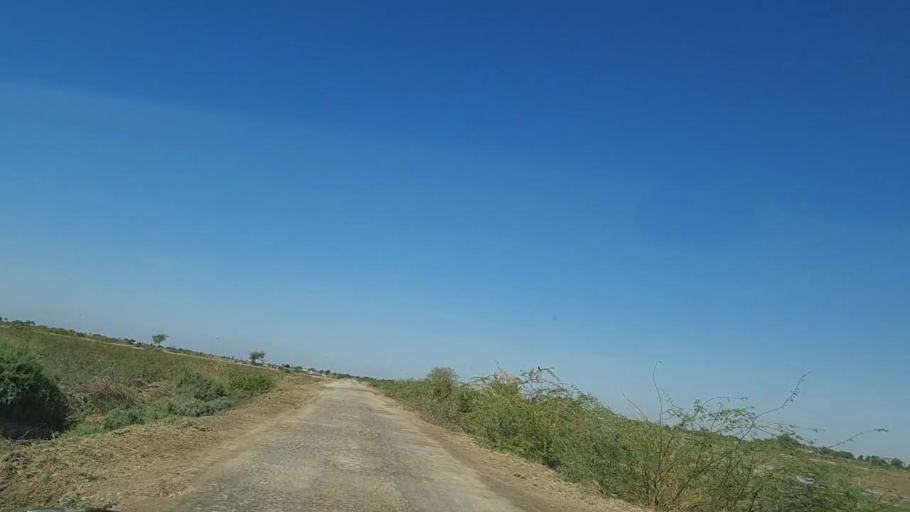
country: PK
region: Sindh
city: Dhoro Naro
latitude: 25.5419
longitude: 69.4996
